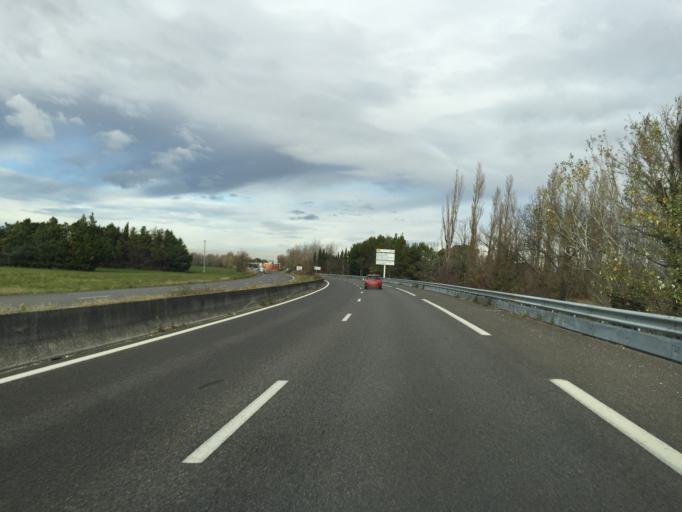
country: FR
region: Provence-Alpes-Cote d'Azur
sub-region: Departement du Vaucluse
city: Althen-des-Paluds
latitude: 44.0007
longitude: 4.9423
